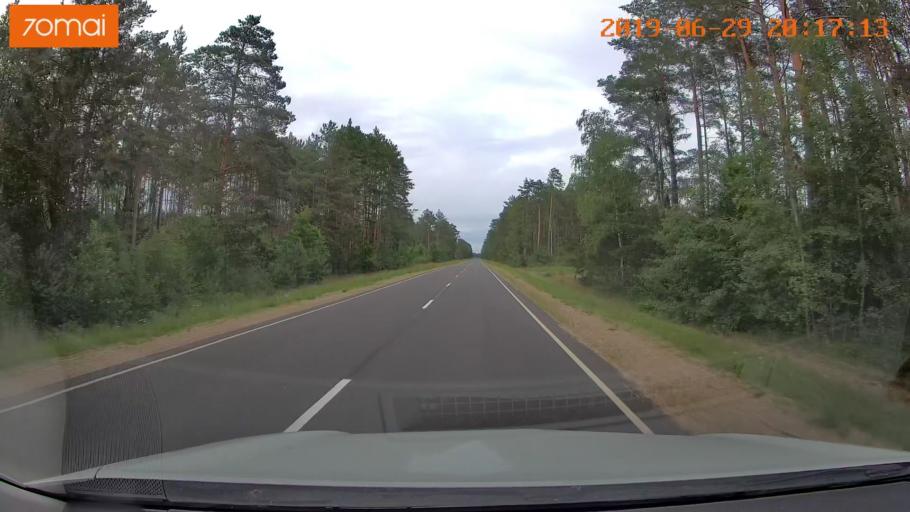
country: BY
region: Brest
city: Asnyezhytsy
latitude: 52.3865
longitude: 26.2118
